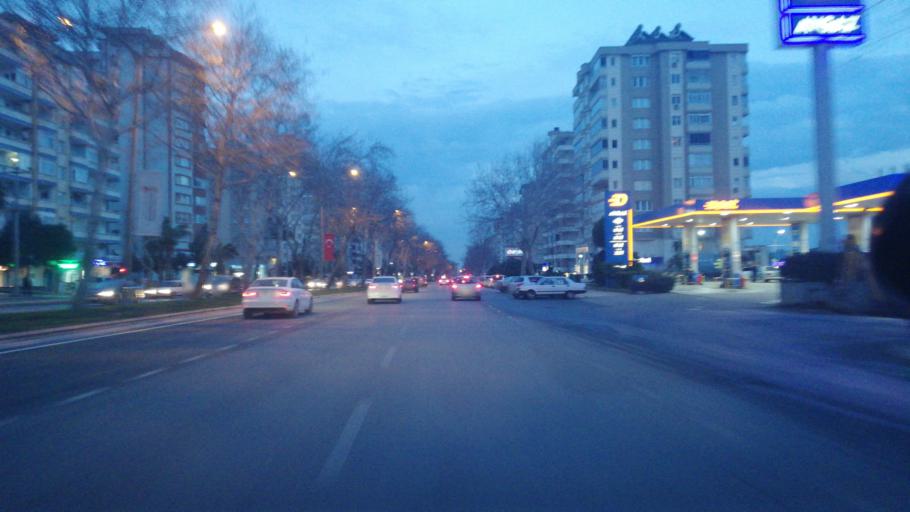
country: TR
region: Kahramanmaras
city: Kahramanmaras
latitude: 37.5882
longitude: 36.8879
